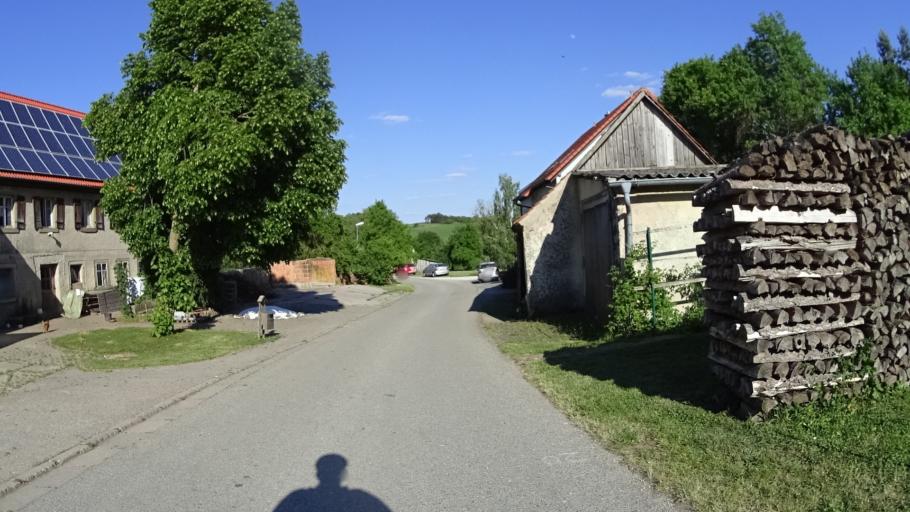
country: DE
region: Bavaria
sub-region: Regierungsbezirk Mittelfranken
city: Feuchtwangen
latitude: 49.1627
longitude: 10.3560
